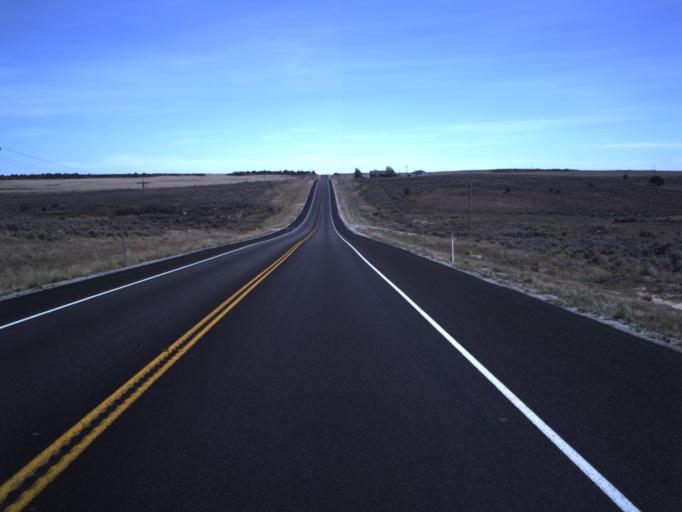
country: US
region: Utah
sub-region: San Juan County
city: Monticello
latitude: 37.8707
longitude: -109.2540
